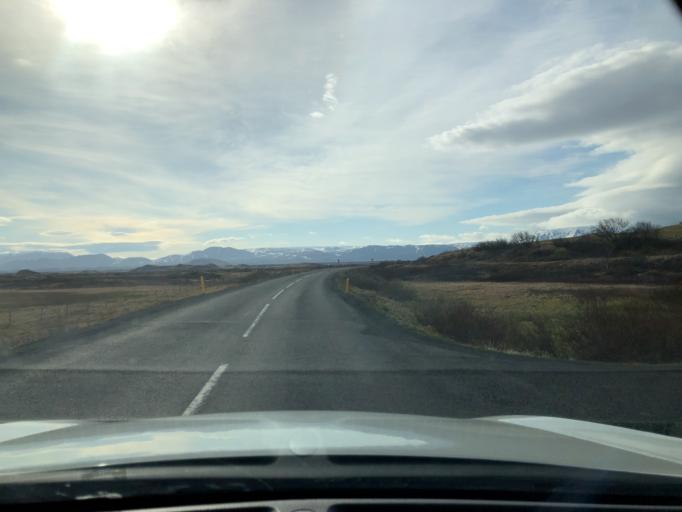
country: IS
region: Northeast
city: Laugar
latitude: 65.5661
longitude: -17.0266
